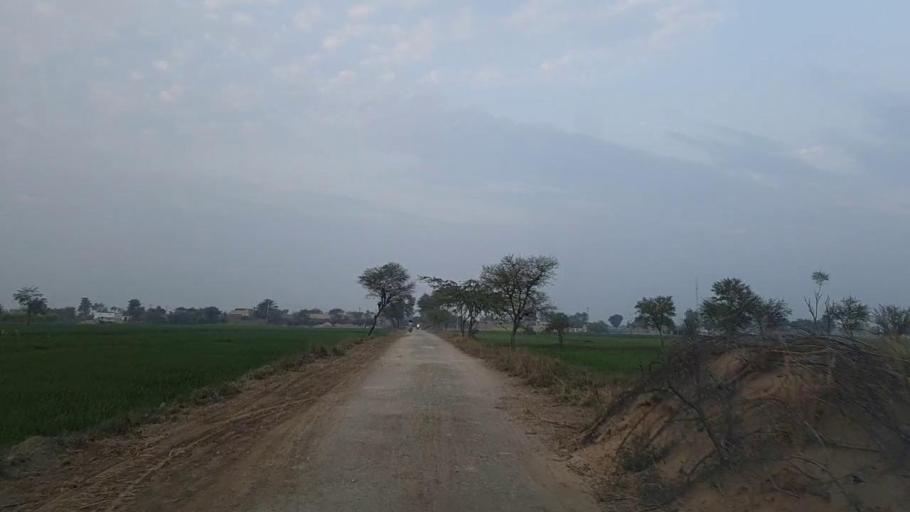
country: PK
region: Sindh
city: Jam Sahib
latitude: 26.2964
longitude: 68.5934
